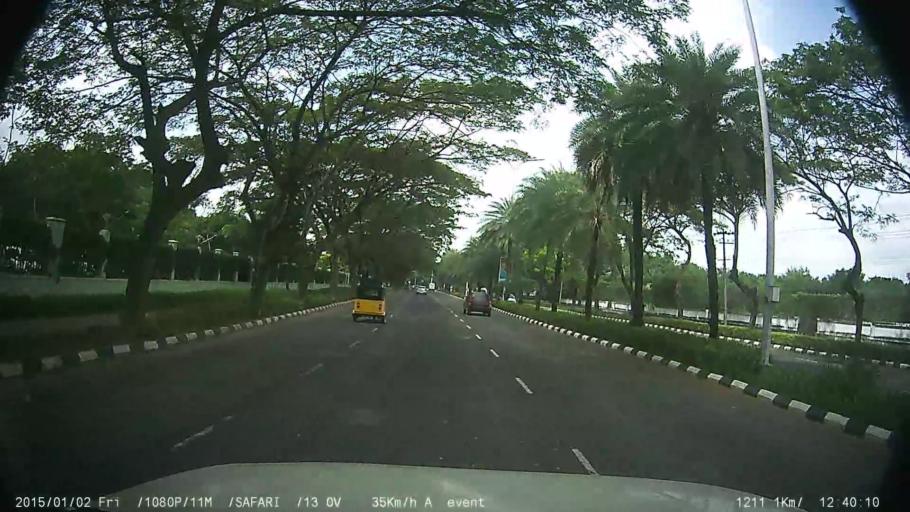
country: IN
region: Tamil Nadu
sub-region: Kancheepuram
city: Singapperumalkovil
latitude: 12.7349
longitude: 80.0096
